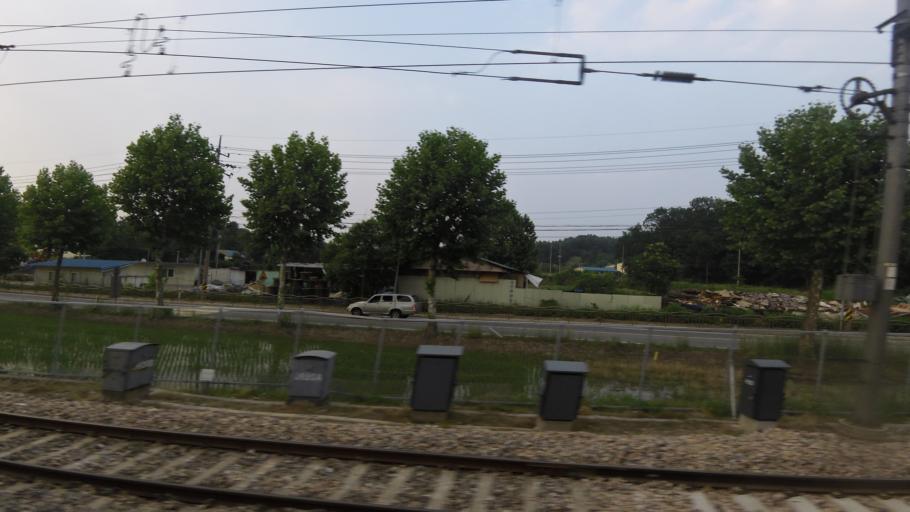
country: KR
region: Daejeon
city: Songgang-dong
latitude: 36.5547
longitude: 127.3265
